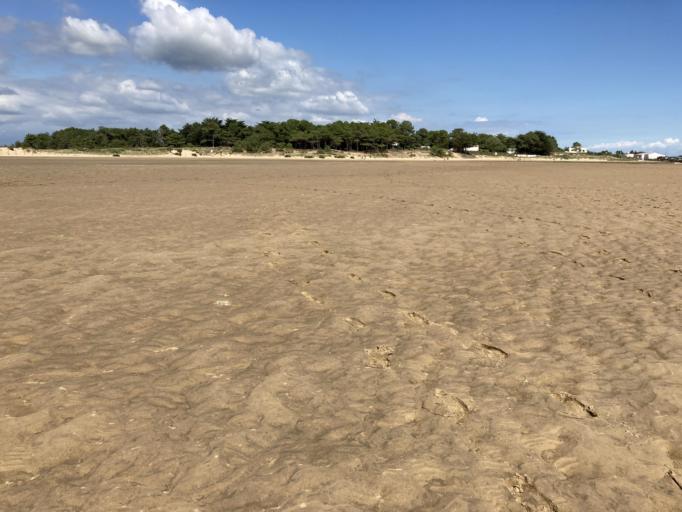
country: FR
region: Pays de la Loire
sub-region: Departement de la Vendee
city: Saint-Hilaire-de-Talmont
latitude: 46.4336
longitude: -1.6429
